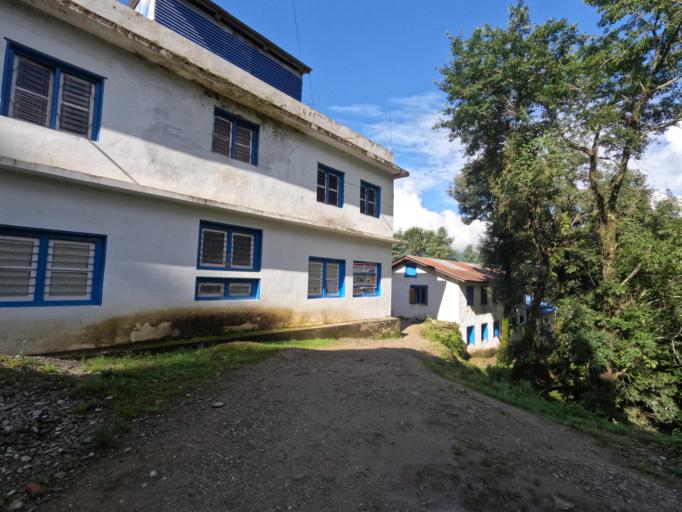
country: NP
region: Eastern Region
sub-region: Sagarmatha Zone
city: Namche Bazar
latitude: 27.4941
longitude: 86.5839
